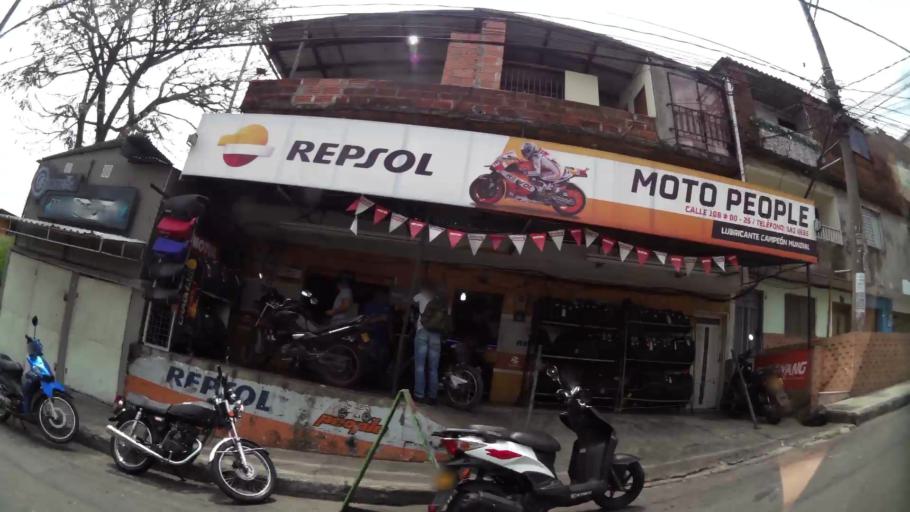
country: CO
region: Antioquia
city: Bello
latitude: 6.3086
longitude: -75.5767
